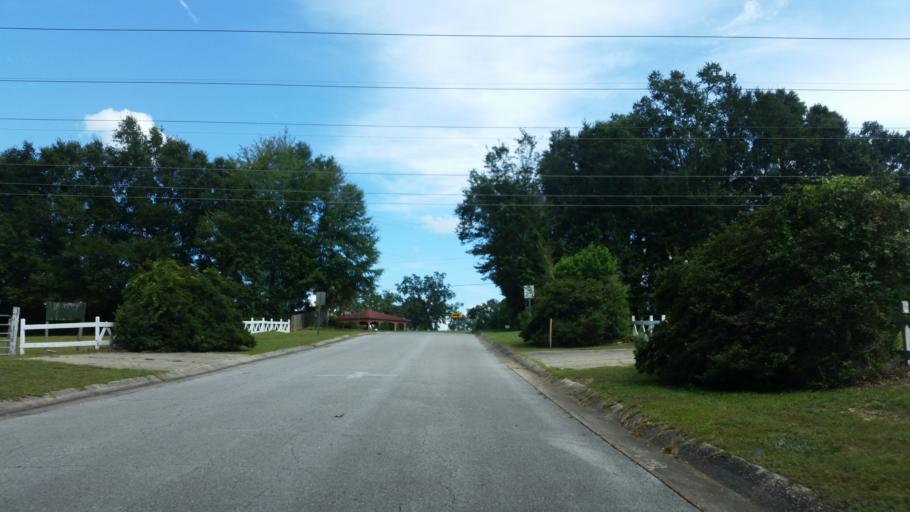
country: US
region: Florida
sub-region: Escambia County
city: Ferry Pass
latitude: 30.5425
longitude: -87.2376
